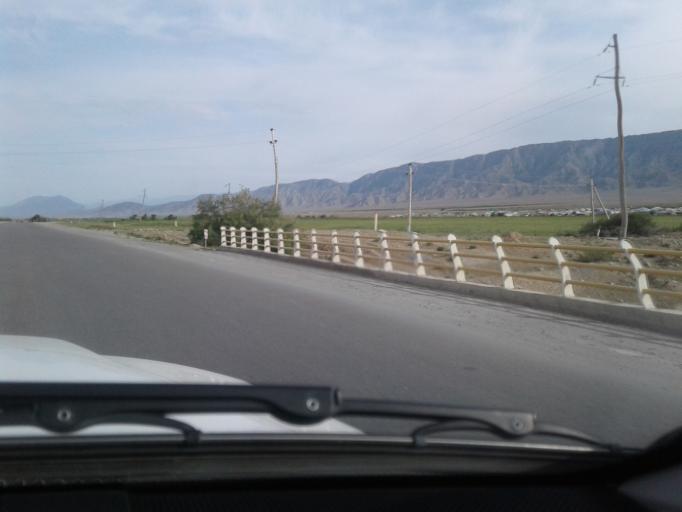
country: TM
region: Ahal
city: Arcabil
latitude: 38.2106
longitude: 57.8130
